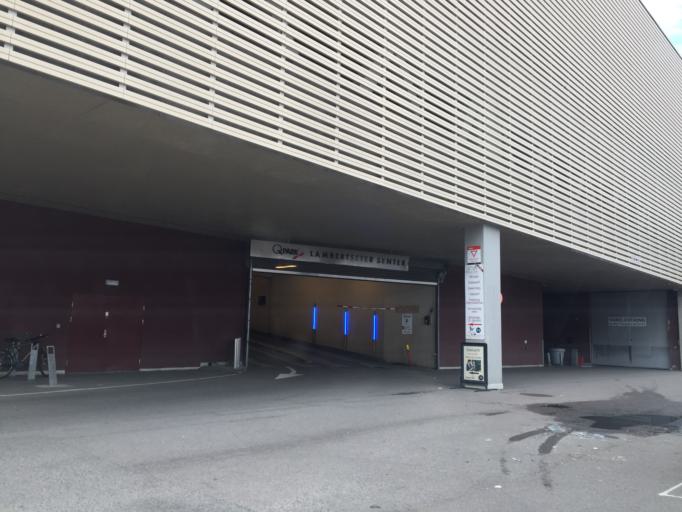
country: NO
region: Akershus
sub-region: Oppegard
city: Kolbotn
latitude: 59.8751
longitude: 10.8108
